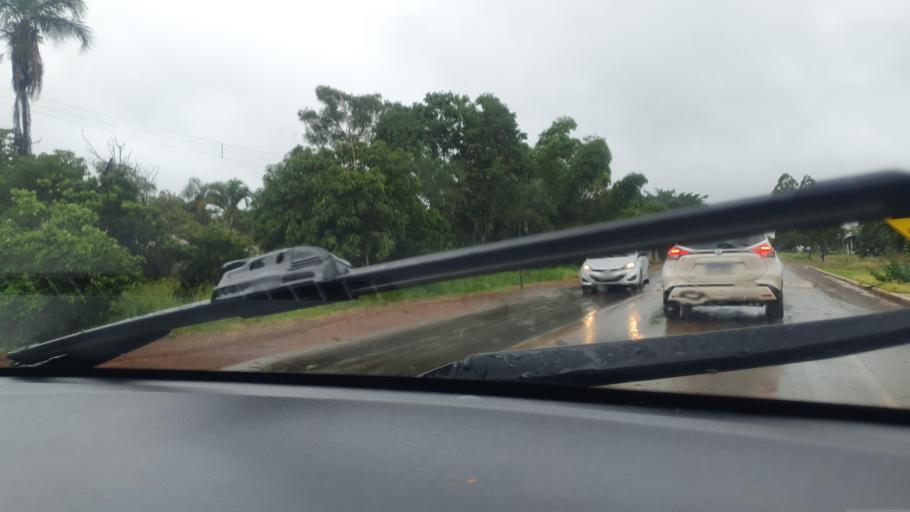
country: BR
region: Goias
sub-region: Vianopolis
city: Vianopolis
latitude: -16.7247
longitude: -48.4328
